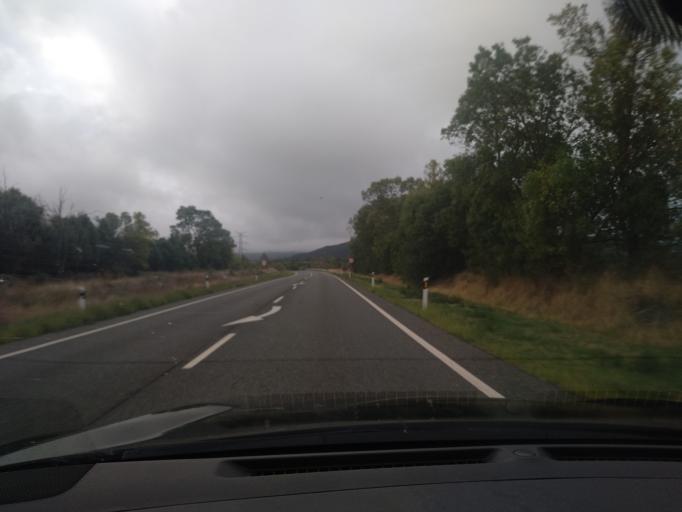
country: ES
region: Castille and Leon
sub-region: Provincia de Segovia
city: Otero de Herreros
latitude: 40.7489
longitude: -4.1994
